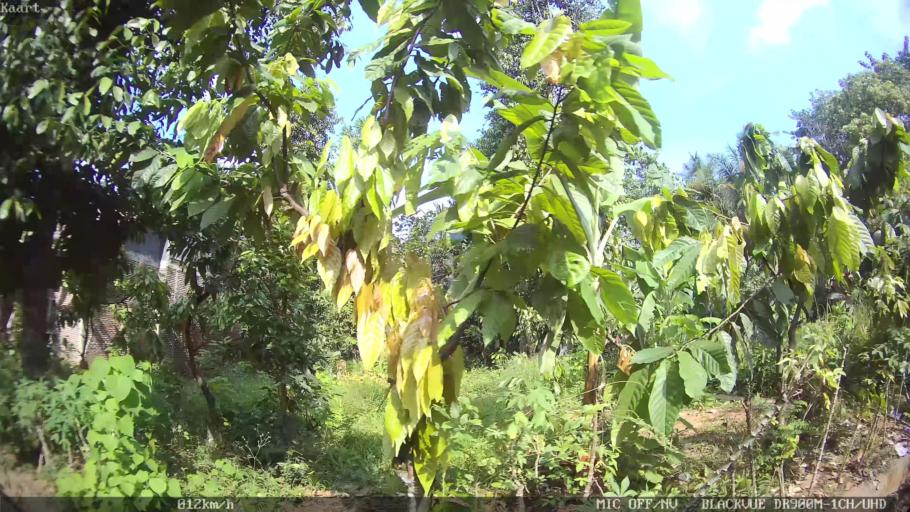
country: ID
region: Lampung
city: Kedaton
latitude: -5.3839
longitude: 105.2251
